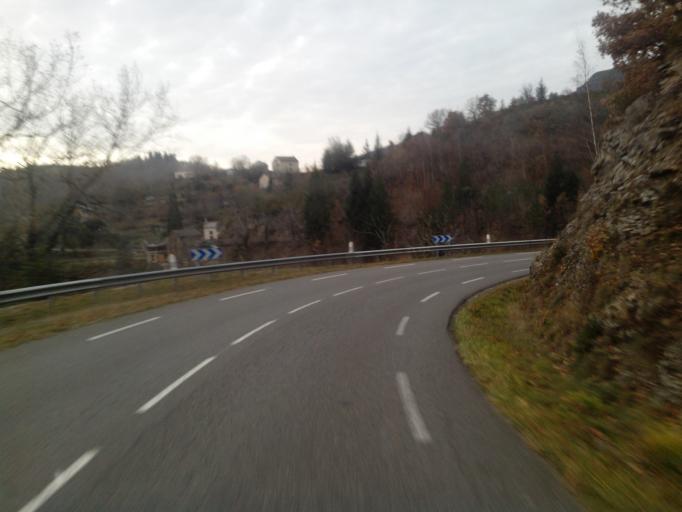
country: FR
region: Languedoc-Roussillon
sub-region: Departement de la Lozere
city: Florac
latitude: 44.2894
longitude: 3.5961
